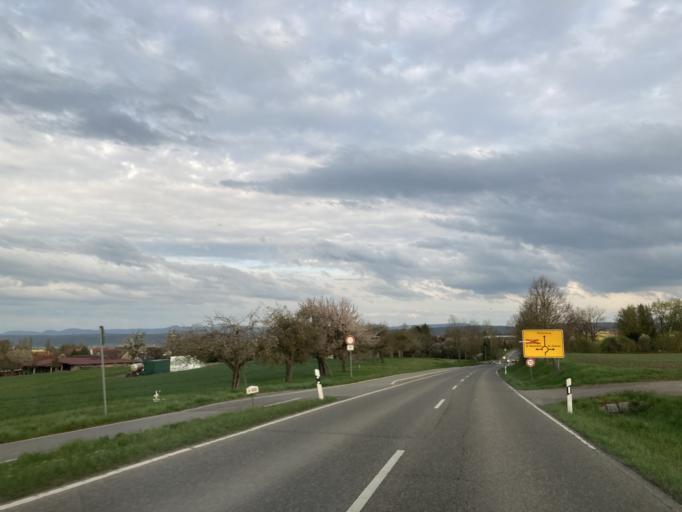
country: DE
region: Baden-Wuerttemberg
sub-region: Tuebingen Region
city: Rottenburg
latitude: 48.5075
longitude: 8.9299
